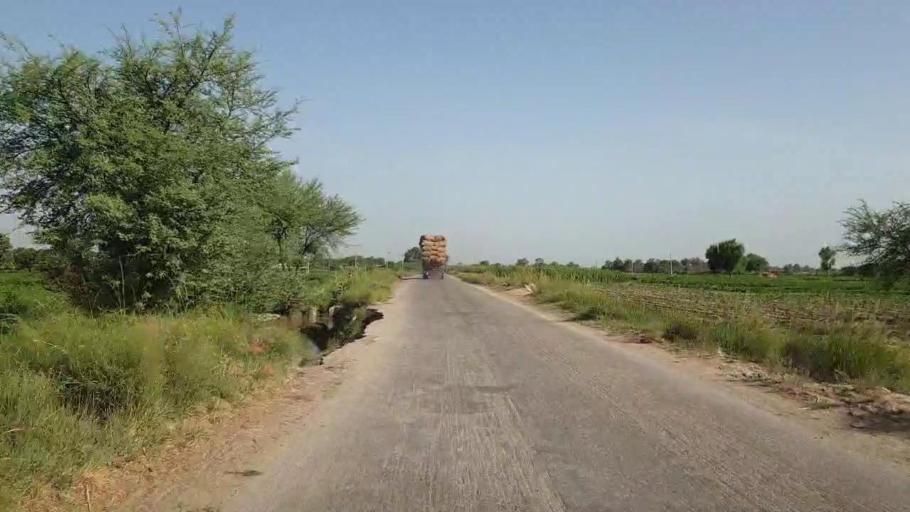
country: PK
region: Sindh
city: Nawabshah
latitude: 26.0966
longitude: 68.4696
